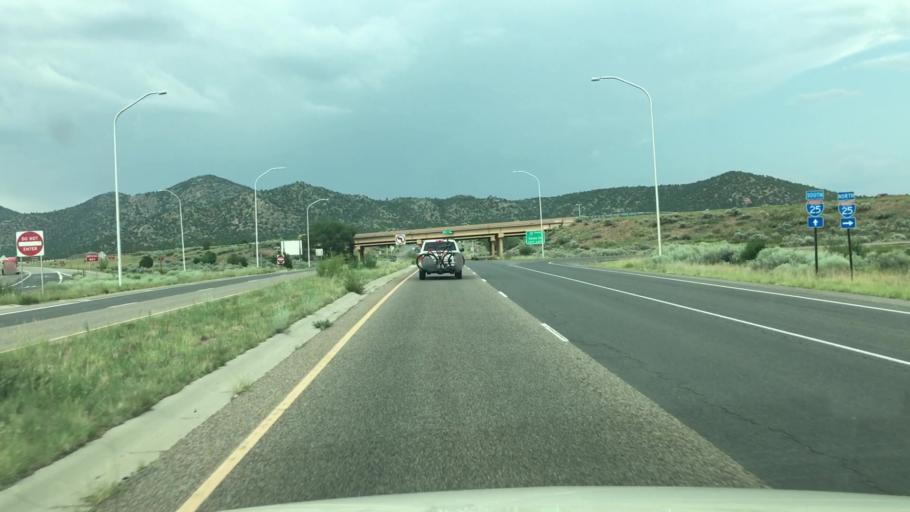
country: US
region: New Mexico
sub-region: Santa Fe County
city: Eldorado at Santa Fe
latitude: 35.5526
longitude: -105.8799
